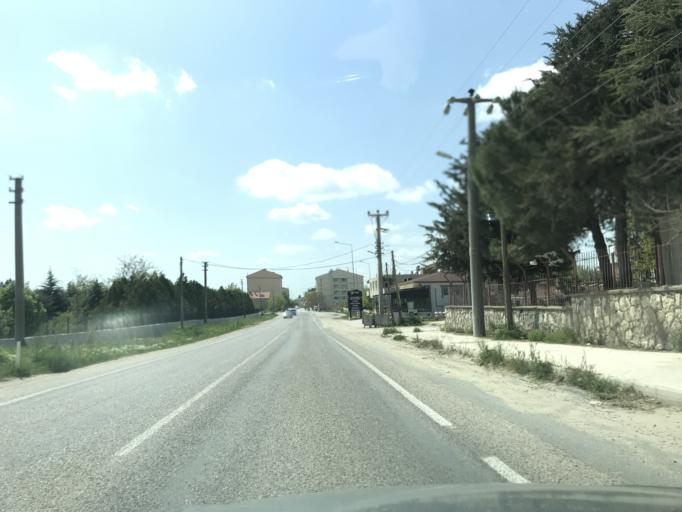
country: TR
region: Kirklareli
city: Pinarhisar
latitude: 41.6227
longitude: 27.5305
